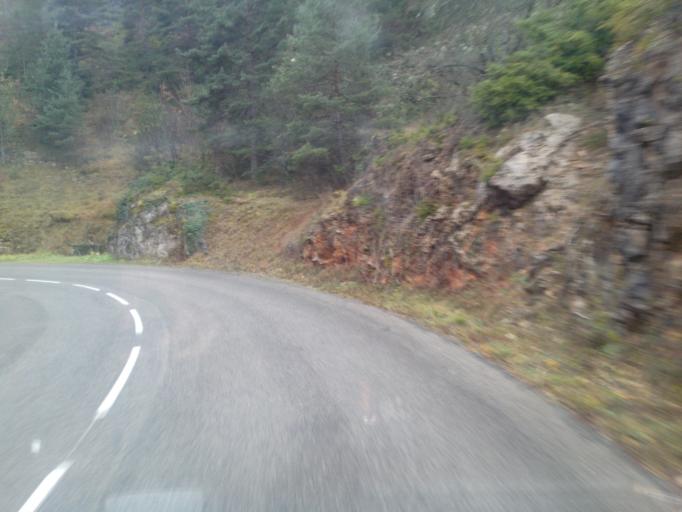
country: FR
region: Languedoc-Roussillon
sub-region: Departement de la Lozere
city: Chanac
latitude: 44.3237
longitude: 3.3454
